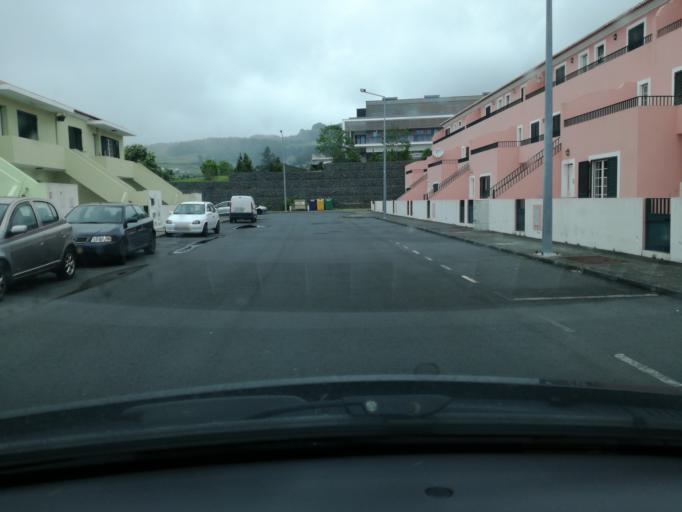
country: PT
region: Azores
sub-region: Angra do Heroismo
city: Angra do Heroismo
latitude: 38.6704
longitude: -27.2143
